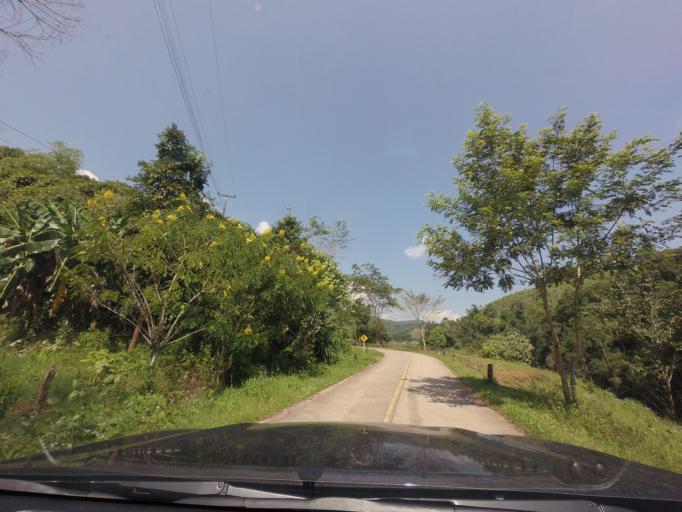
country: TH
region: Nan
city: Bo Kluea
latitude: 19.1970
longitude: 101.1882
